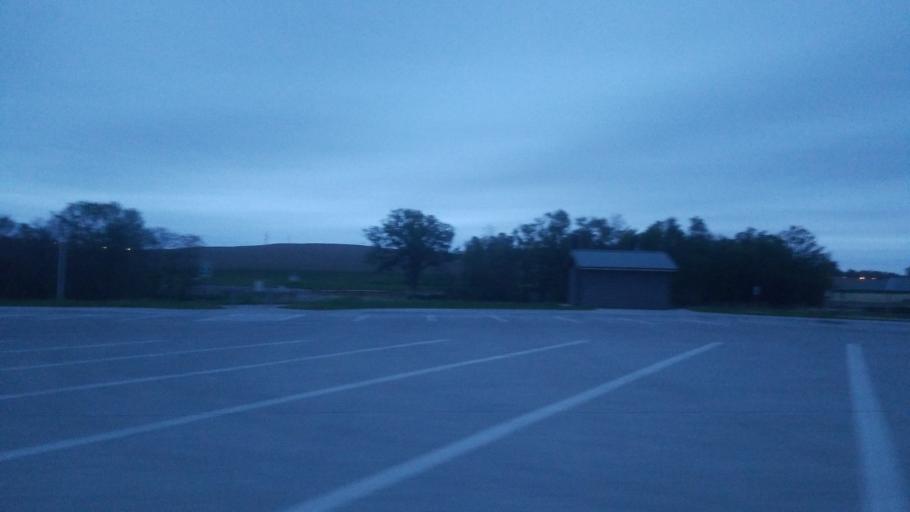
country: US
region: Nebraska
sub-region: Sarpy County
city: Chalco
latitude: 41.1646
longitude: -96.0991
